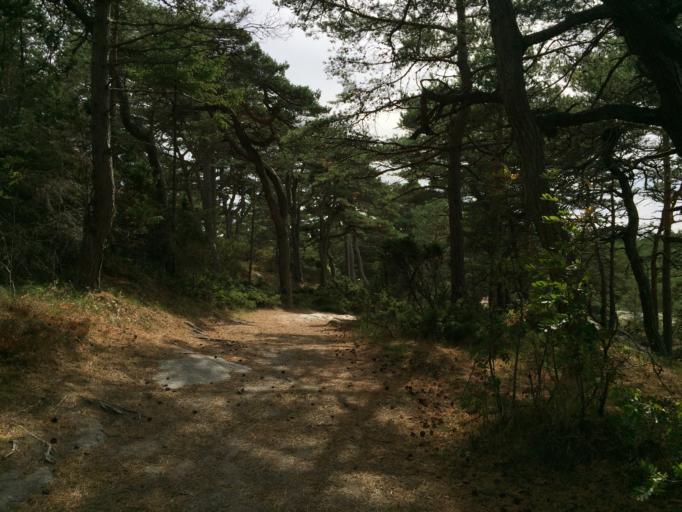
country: NO
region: Ostfold
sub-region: Hvaler
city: Skjaerhalden
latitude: 59.0230
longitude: 11.0185
